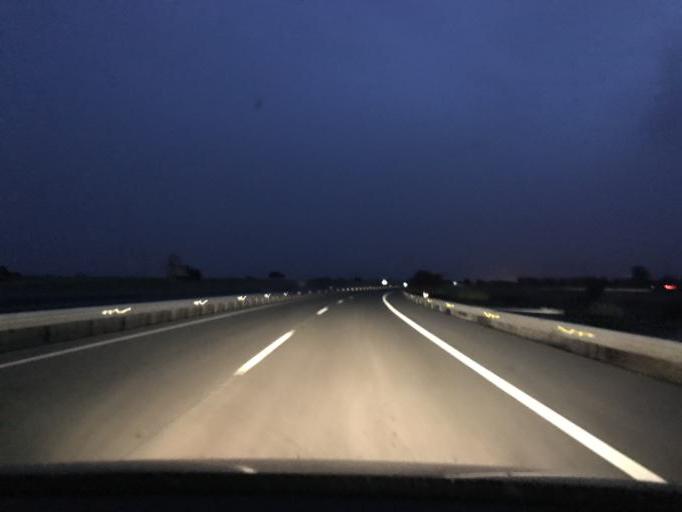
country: ES
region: Andalusia
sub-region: Provincia de Granada
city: Benalua de Guadix
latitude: 37.3693
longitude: -3.0719
